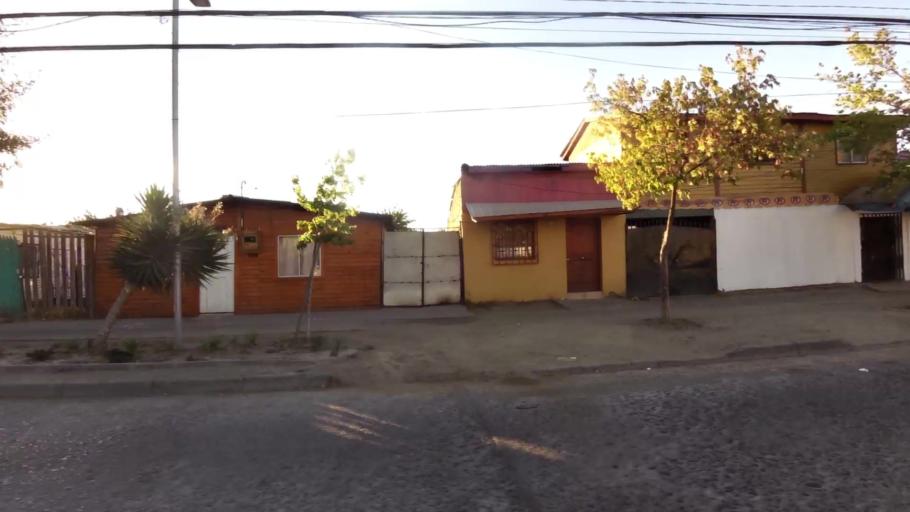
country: CL
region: O'Higgins
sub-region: Provincia de Cachapoal
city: Rancagua
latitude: -34.1693
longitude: -70.7609
